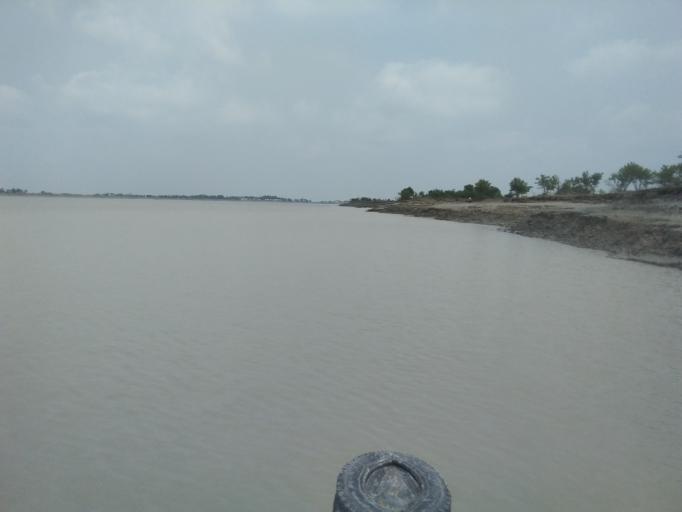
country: BD
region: Khulna
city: Phultala
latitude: 22.6458
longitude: 89.4108
